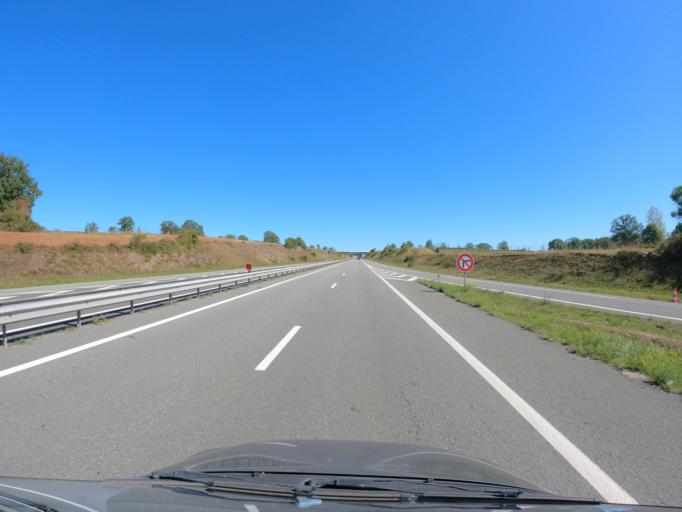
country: FR
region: Limousin
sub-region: Departement de la Creuse
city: Gouzon
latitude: 46.1960
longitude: 2.1530
